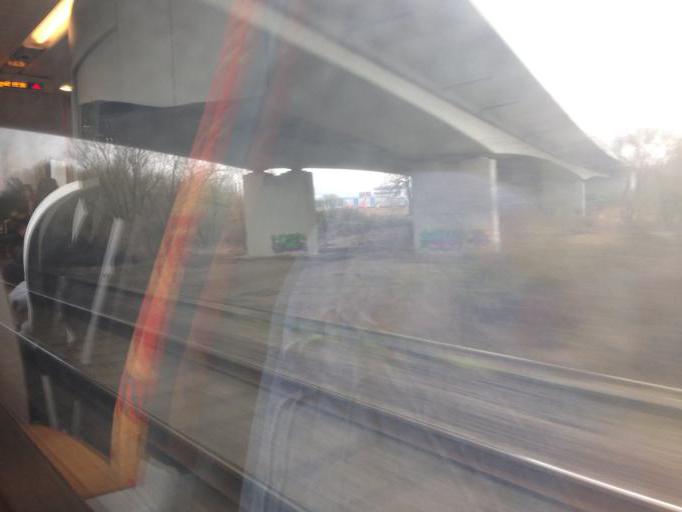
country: DE
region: Hesse
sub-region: Regierungsbezirk Giessen
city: Asslar
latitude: 50.5812
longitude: 8.4834
